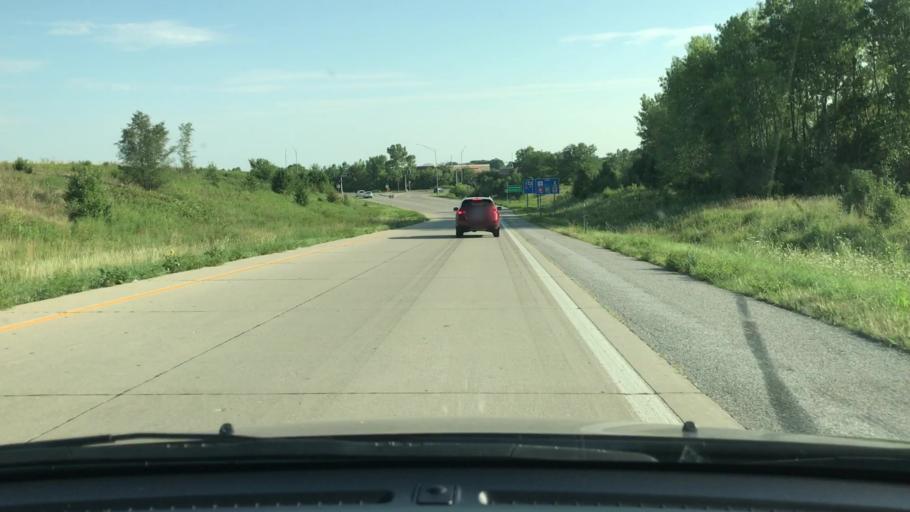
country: US
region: Missouri
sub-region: Cass County
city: Lake Winnebago
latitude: 38.8549
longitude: -94.3763
